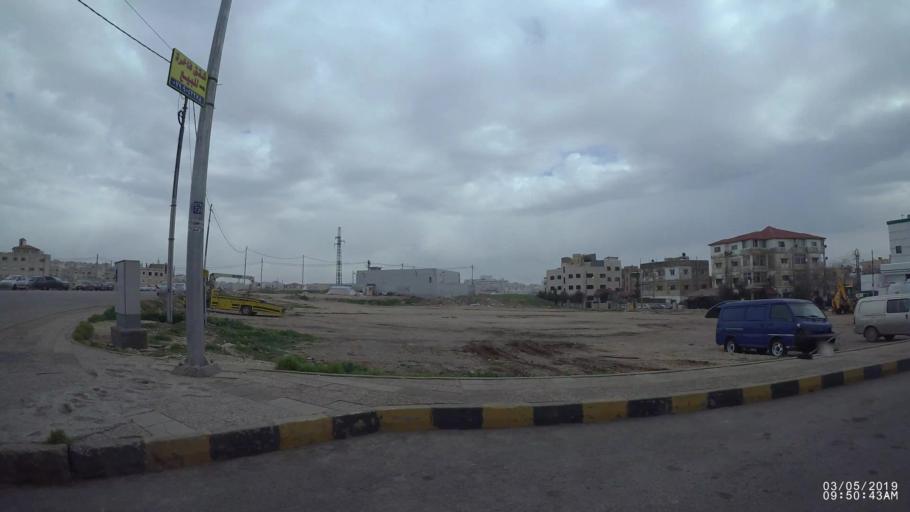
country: JO
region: Amman
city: Amman
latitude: 31.9761
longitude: 35.9301
